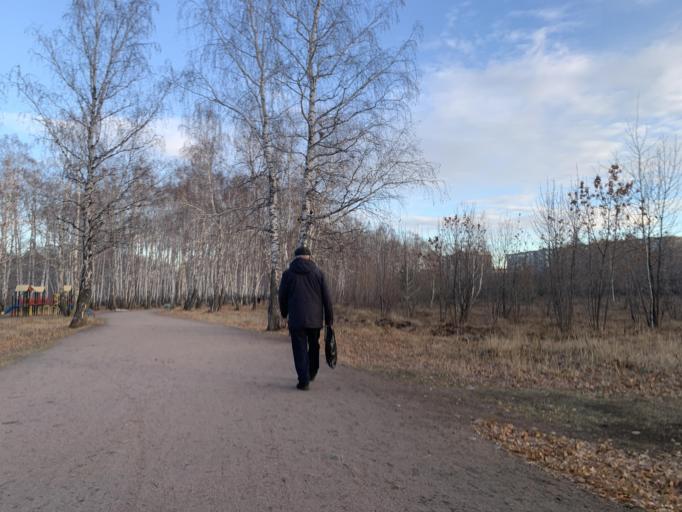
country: RU
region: Chelyabinsk
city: Roshchino
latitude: 55.2007
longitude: 61.3072
